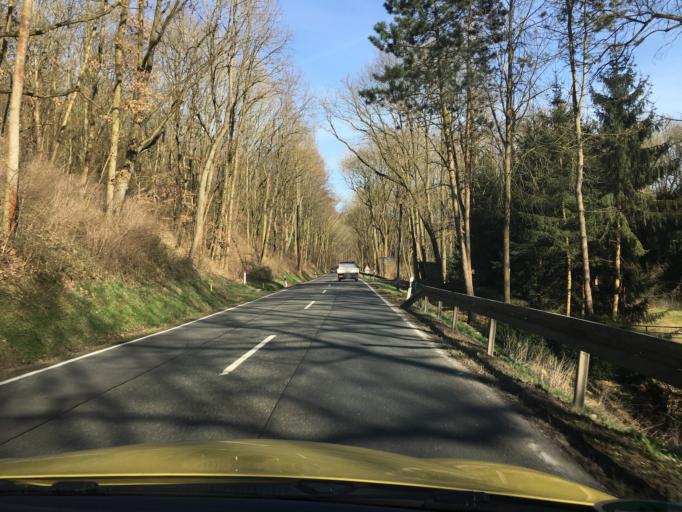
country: DE
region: Saxony-Anhalt
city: Bad Bibra
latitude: 51.2138
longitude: 11.5375
